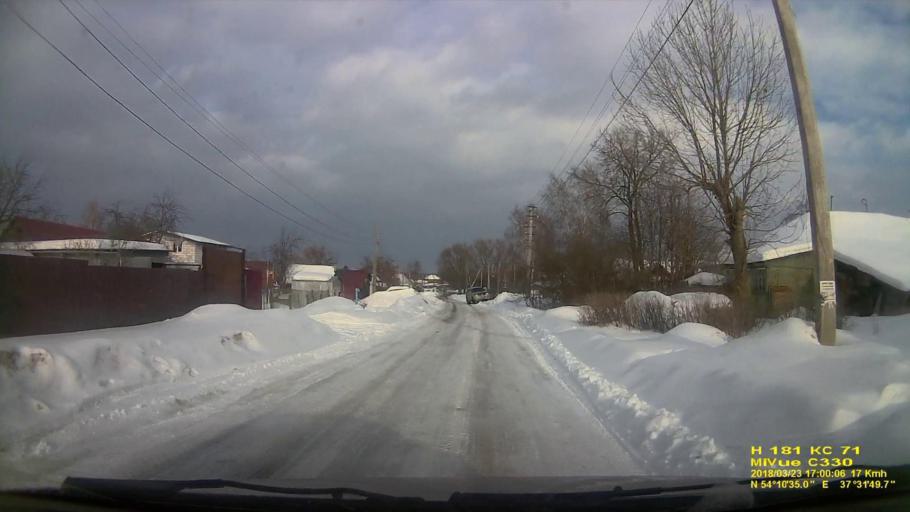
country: RU
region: Tula
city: Kosaya Gora
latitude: 54.1764
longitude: 37.5306
